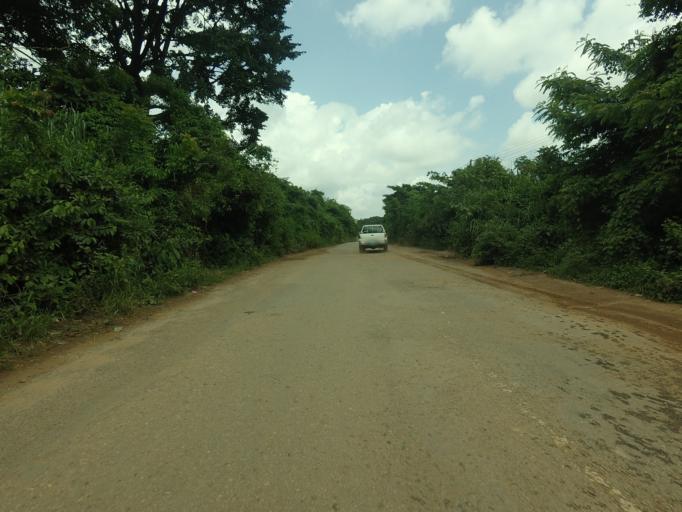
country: GH
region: Volta
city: Ho
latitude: 6.7296
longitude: 0.3460
